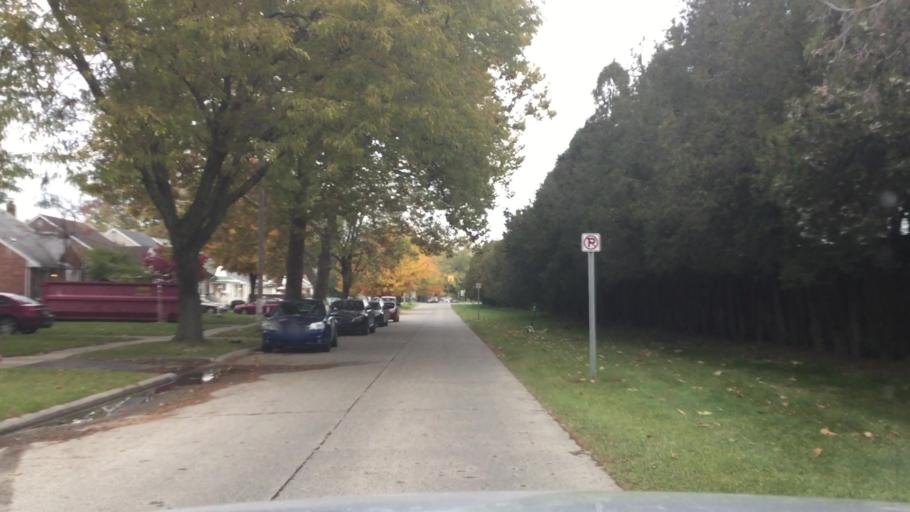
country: US
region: Michigan
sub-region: Wayne County
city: Dearborn Heights
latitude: 42.3621
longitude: -83.2799
